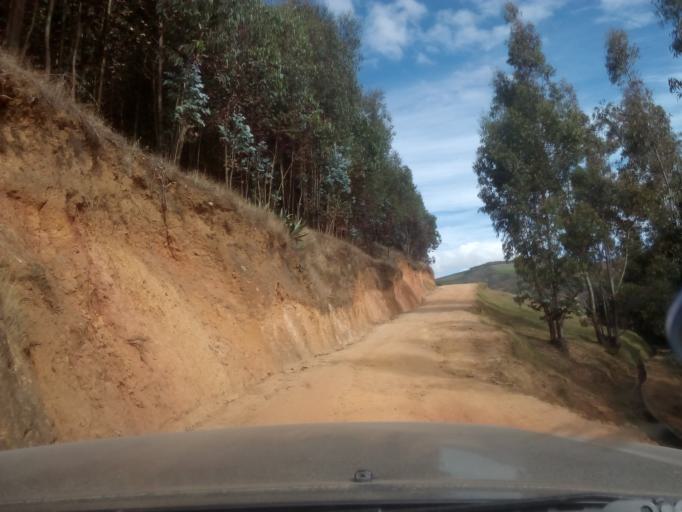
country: PE
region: La Libertad
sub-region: Sanchez Carrion
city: Curgos
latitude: -7.8648
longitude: -77.9436
